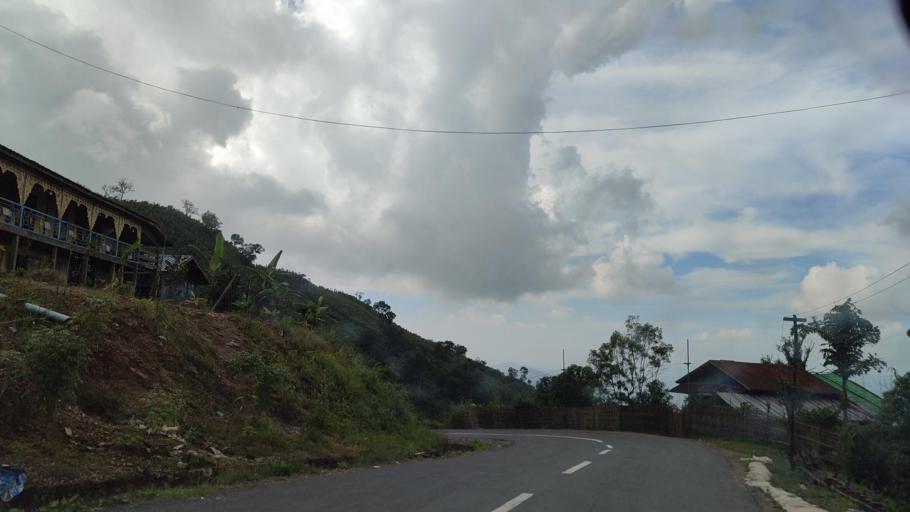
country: MM
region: Magway
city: Minbu
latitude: 19.8219
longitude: 94.2736
